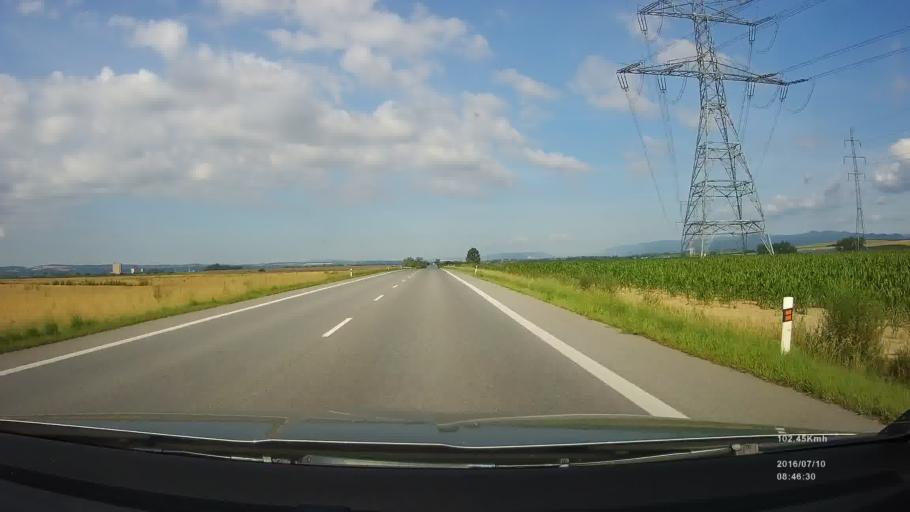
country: SK
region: Kosicky
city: Moldava nad Bodvou
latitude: 48.6041
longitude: 21.0982
